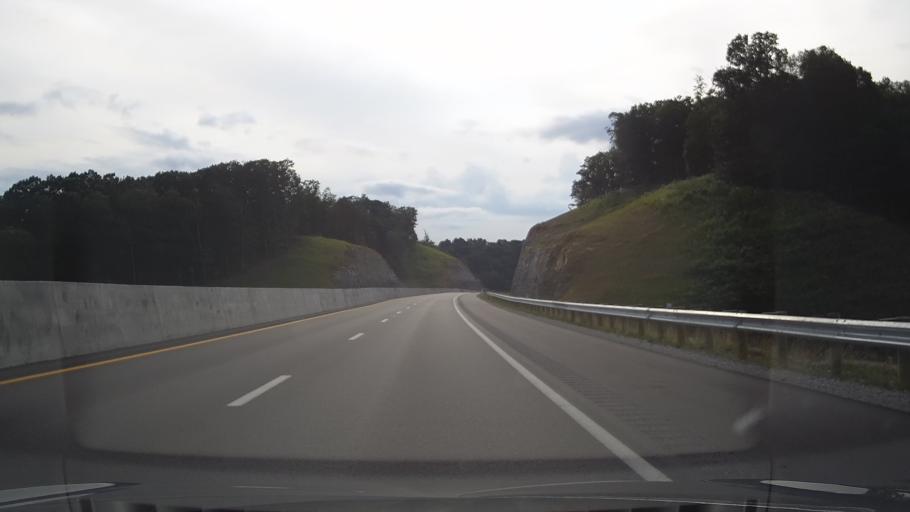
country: US
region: Ohio
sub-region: Scioto County
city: Lucasville
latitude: 38.8685
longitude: -82.9280
